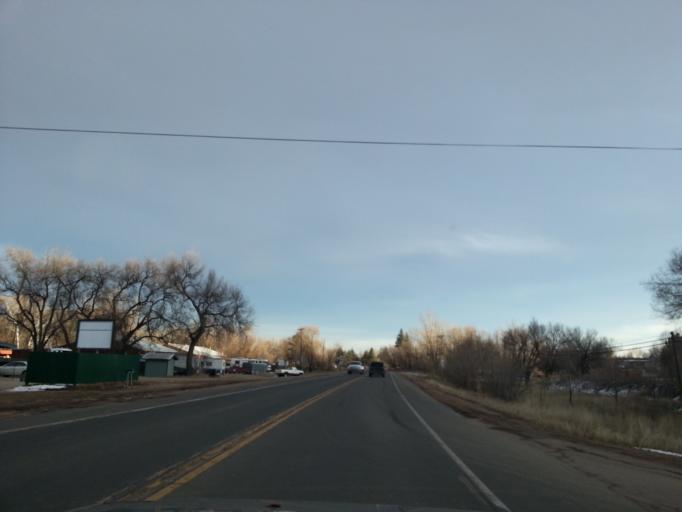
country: US
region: Colorado
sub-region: Larimer County
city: Loveland
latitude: 40.4186
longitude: -105.1761
